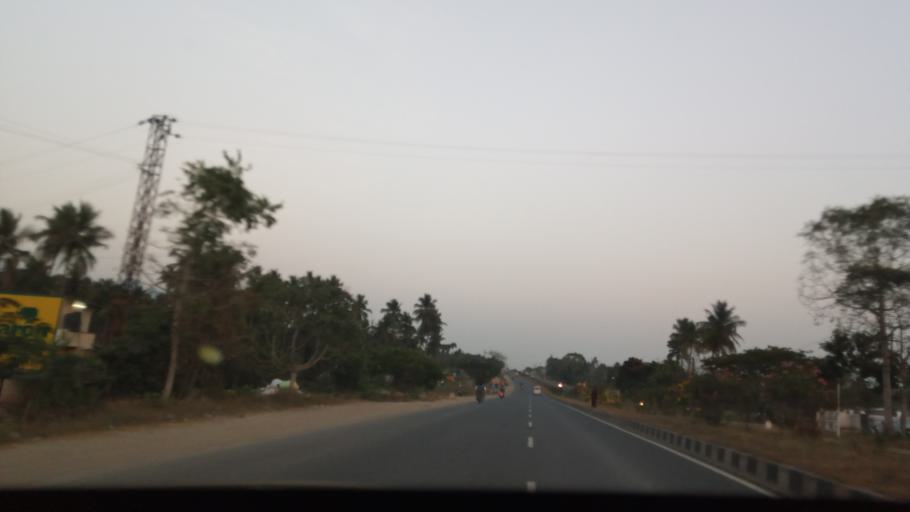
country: IN
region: Tamil Nadu
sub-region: Salem
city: Belur
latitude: 11.6649
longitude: 78.2975
